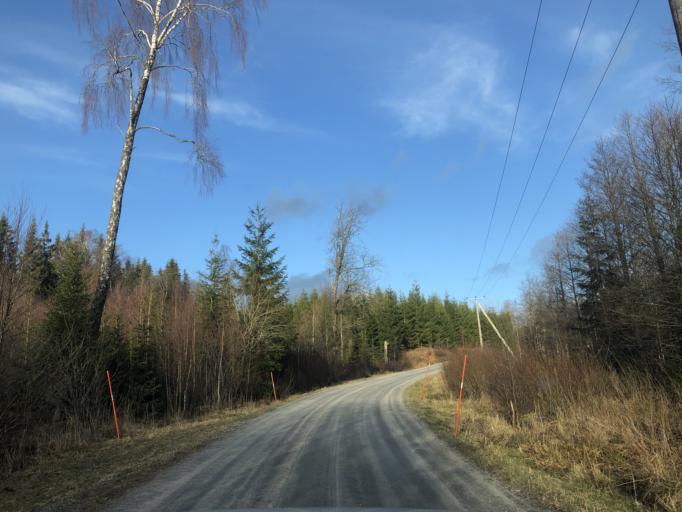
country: SE
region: Vaestra Goetaland
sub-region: Ulricehamns Kommun
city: Ulricehamn
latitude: 57.7620
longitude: 13.4600
